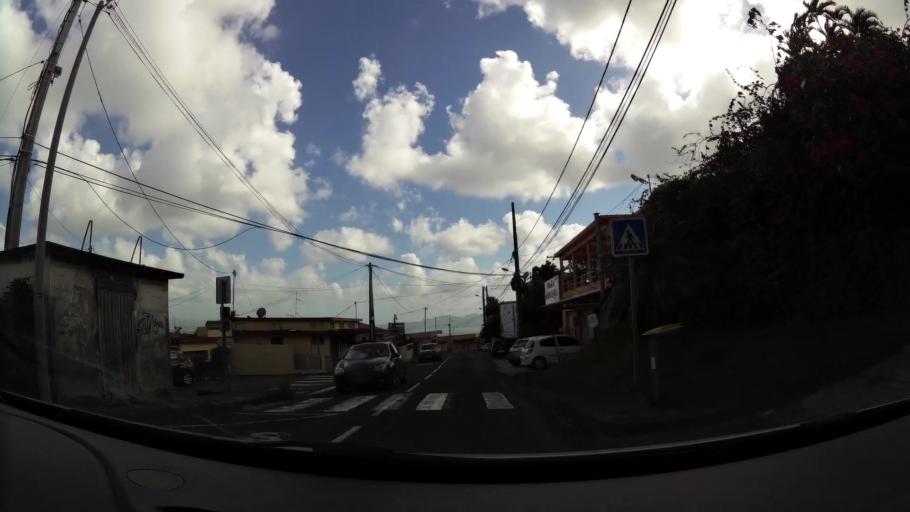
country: MQ
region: Martinique
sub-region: Martinique
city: Fort-de-France
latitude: 14.6223
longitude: -61.0605
